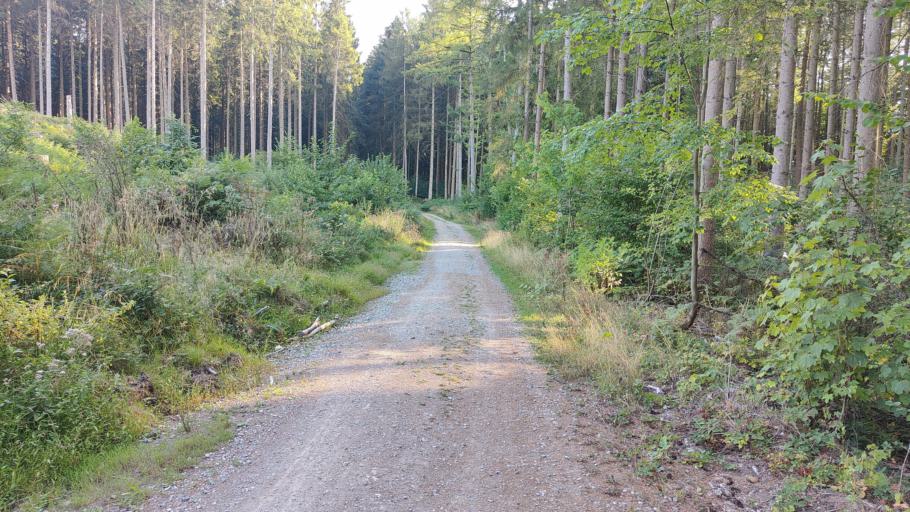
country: BE
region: Wallonia
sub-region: Province de Liege
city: La Calamine
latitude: 50.7312
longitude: 6.0466
